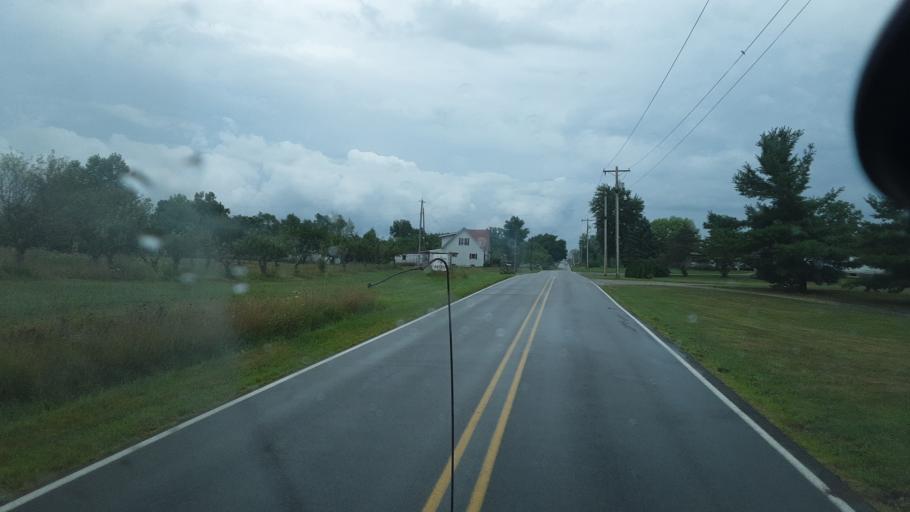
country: US
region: Indiana
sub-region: Steuben County
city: Hamilton
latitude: 41.6229
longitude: -84.8383
